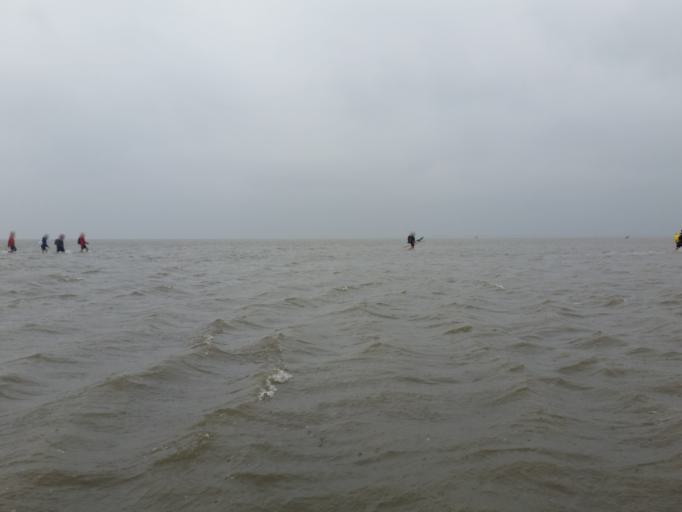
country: NL
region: Friesland
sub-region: Gemeente Dongeradeel
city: Holwerd
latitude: 53.4231
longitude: 5.9084
